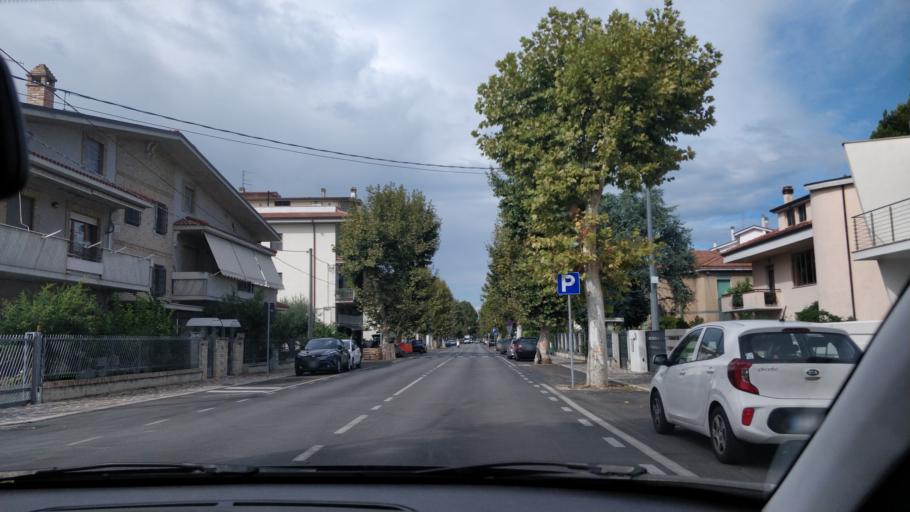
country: IT
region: Abruzzo
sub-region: Provincia di Chieti
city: Sambuceto
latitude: 42.4207
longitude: 14.1821
